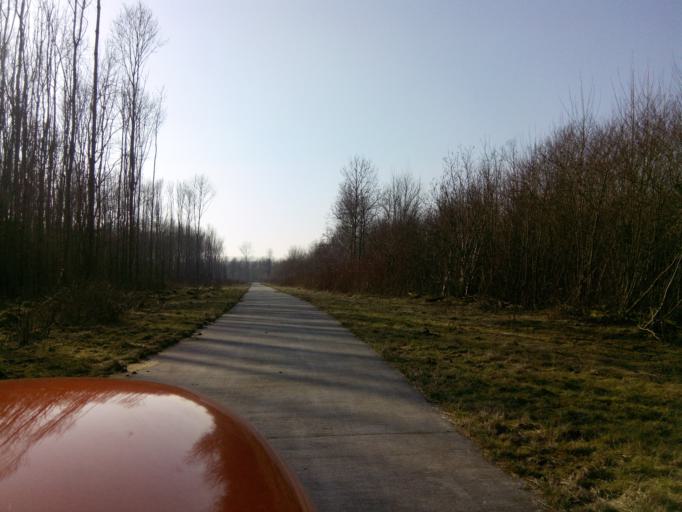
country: NL
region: Flevoland
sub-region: Gemeente Zeewolde
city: Zeewolde
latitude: 52.2898
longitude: 5.4873
